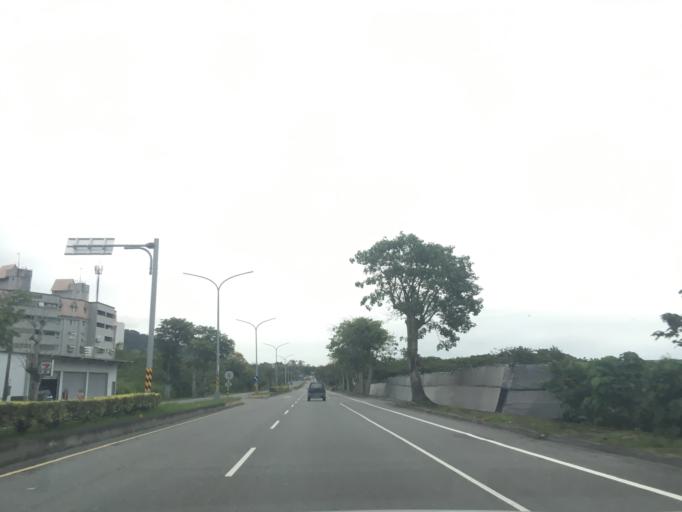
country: TW
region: Taiwan
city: Taitung City
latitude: 22.7078
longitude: 121.0427
